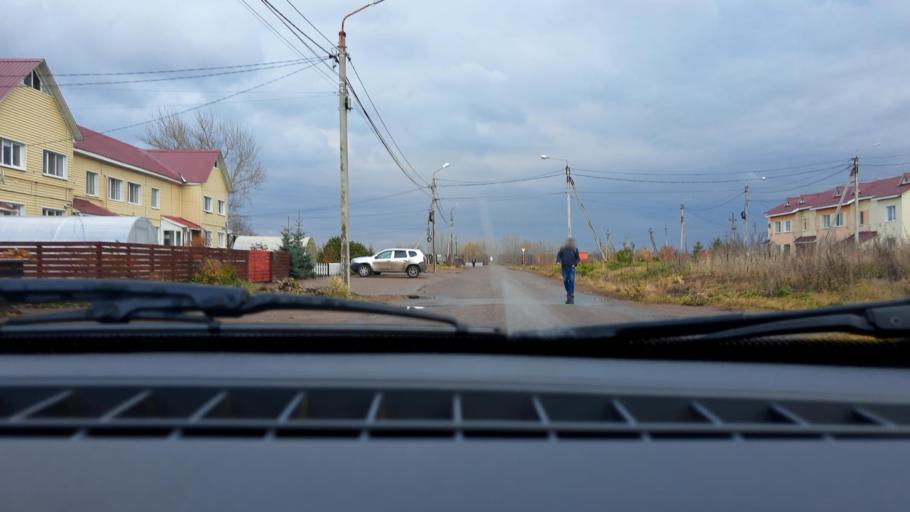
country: RU
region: Bashkortostan
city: Ufa
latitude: 54.8524
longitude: 56.0128
